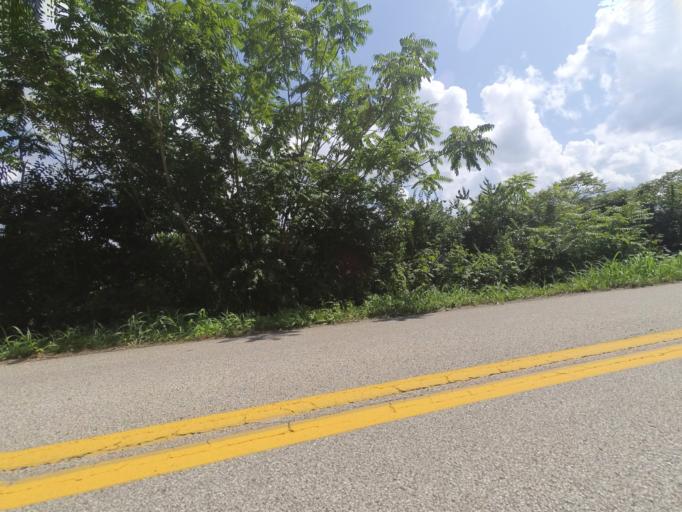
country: US
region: West Virginia
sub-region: Cabell County
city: Pea Ridge
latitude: 38.4264
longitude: -82.3283
